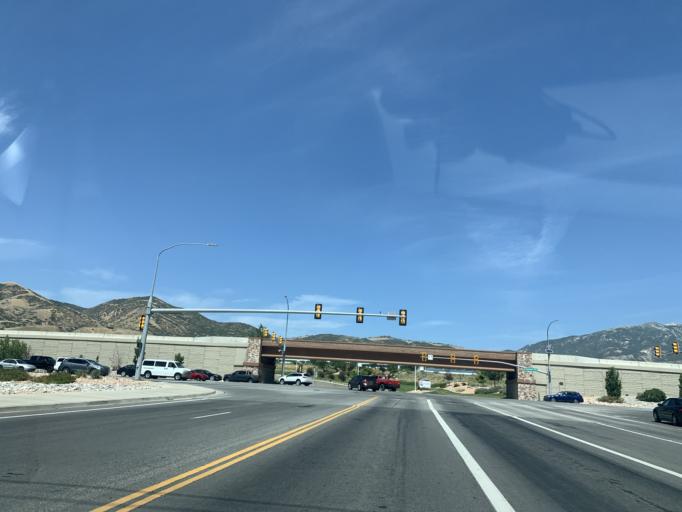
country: US
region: Utah
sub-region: Utah County
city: Lehi
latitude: 40.4315
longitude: -111.8306
